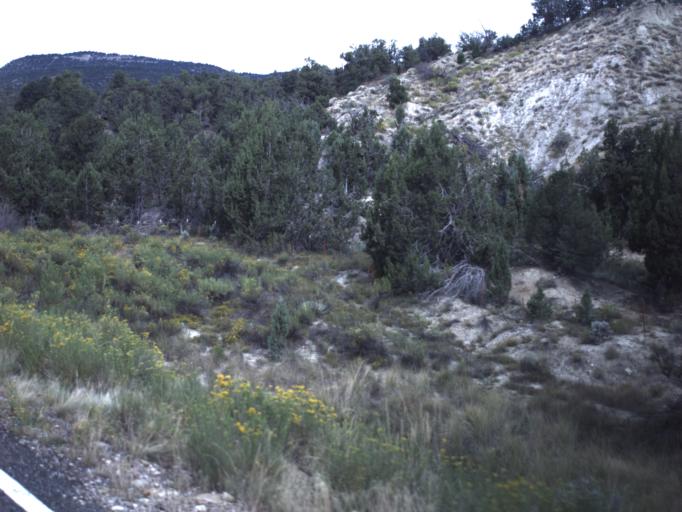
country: US
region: Utah
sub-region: Washington County
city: Hildale
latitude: 37.2621
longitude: -112.7857
